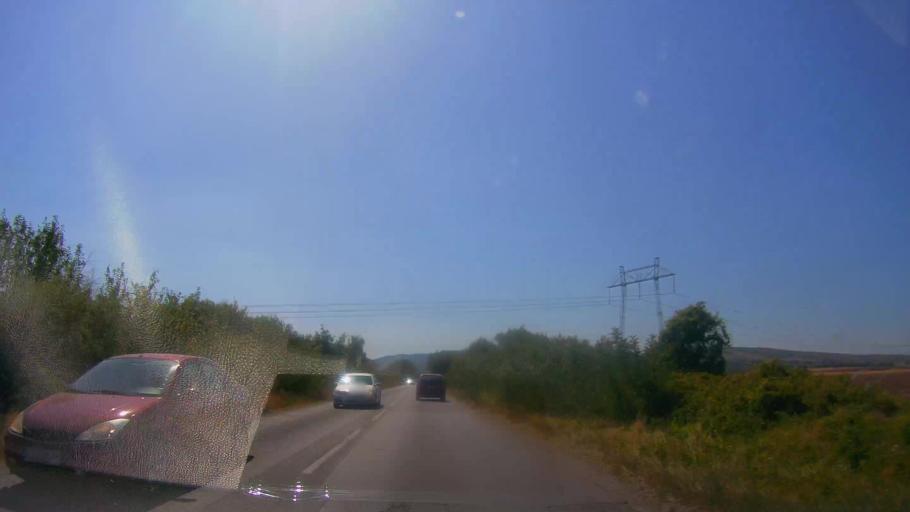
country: BG
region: Veliko Turnovo
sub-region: Obshtina Gorna Oryakhovitsa
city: Purvomaytsi
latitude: 43.1594
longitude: 25.6193
